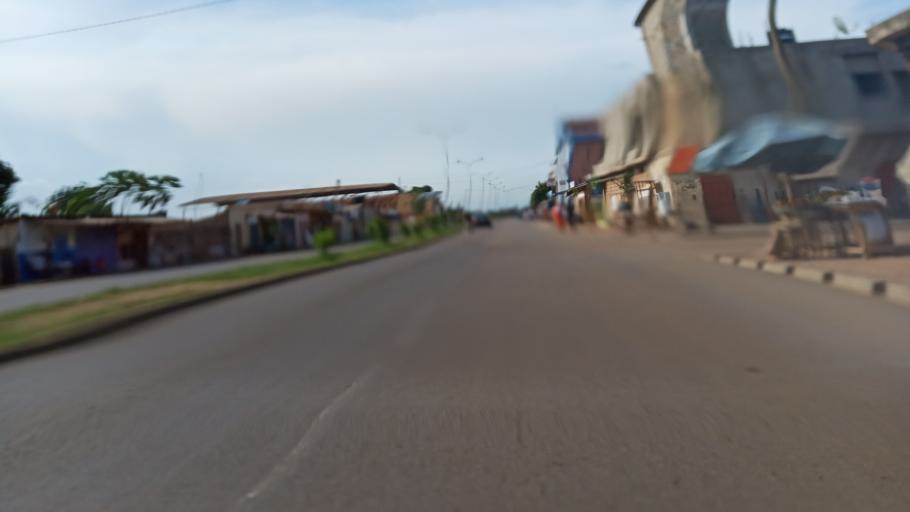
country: TG
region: Maritime
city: Lome
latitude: 6.1766
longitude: 1.2678
